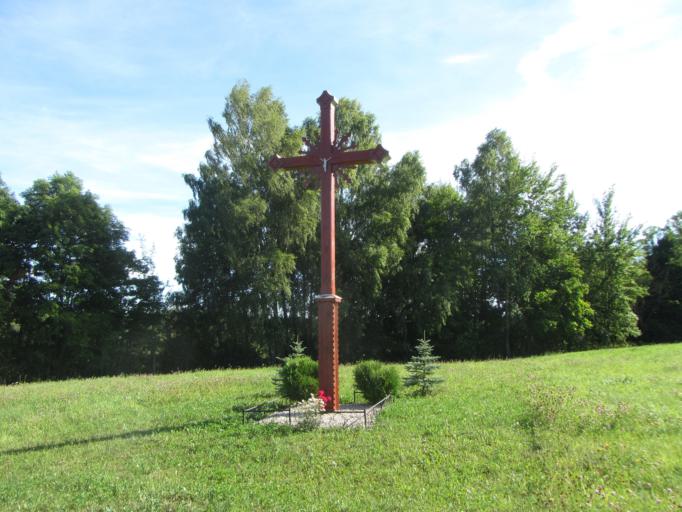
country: LT
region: Panevezys
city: Rokiskis
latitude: 55.7408
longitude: 25.3760
